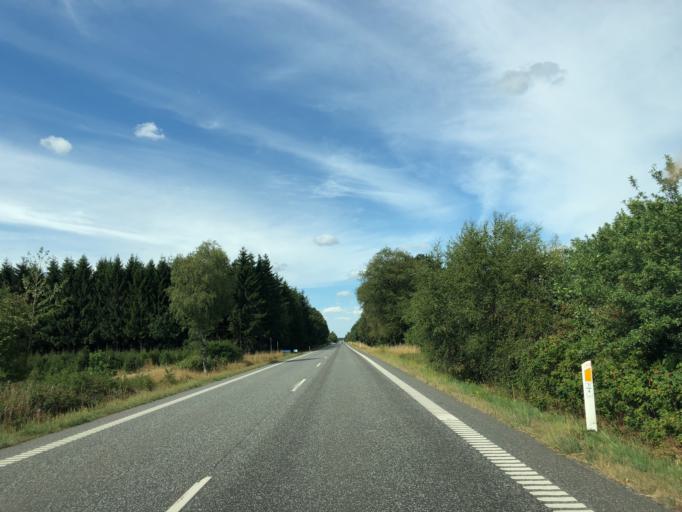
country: DK
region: Central Jutland
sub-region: Ikast-Brande Kommune
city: Bording Kirkeby
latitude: 56.1378
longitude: 9.3750
